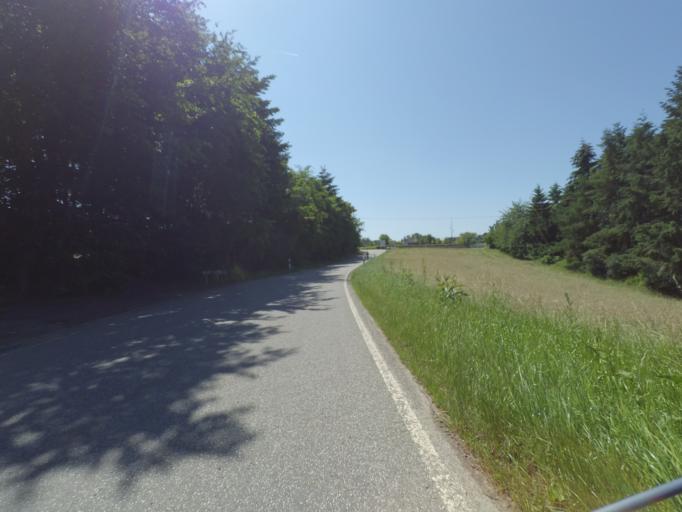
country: DE
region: Rheinland-Pfalz
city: Morsdorf
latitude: 50.1050
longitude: 7.3495
